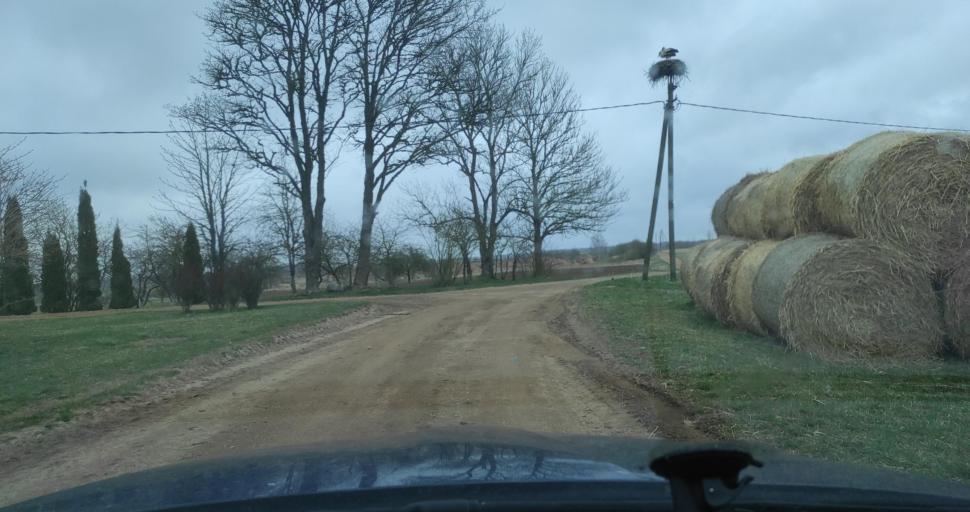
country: LV
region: Broceni
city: Broceni
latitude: 56.7470
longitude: 22.4916
